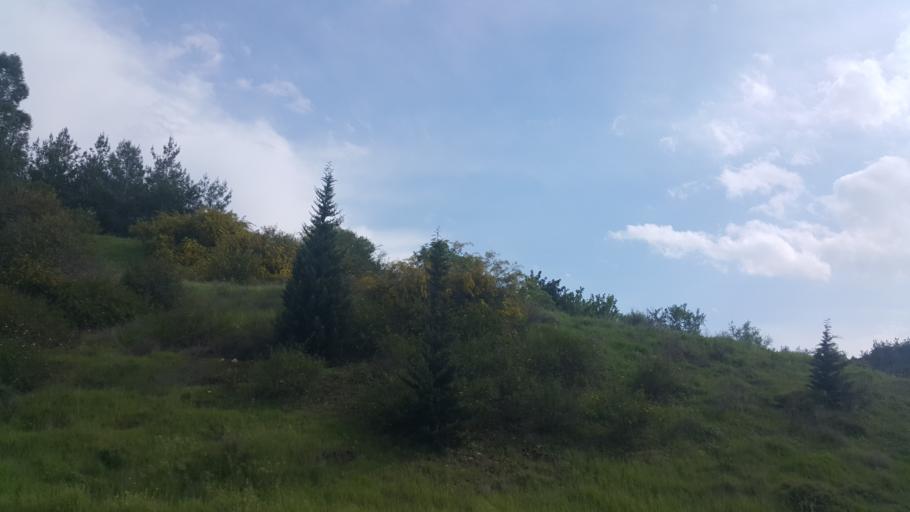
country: TR
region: Mersin
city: Tarsus
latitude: 36.9553
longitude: 34.7542
